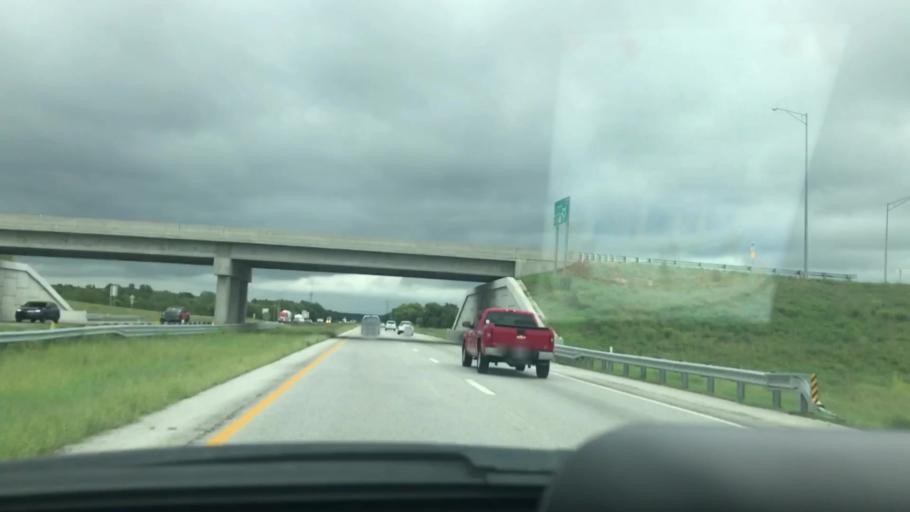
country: US
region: Missouri
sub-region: Jasper County
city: Duenweg
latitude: 37.0689
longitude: -94.4047
